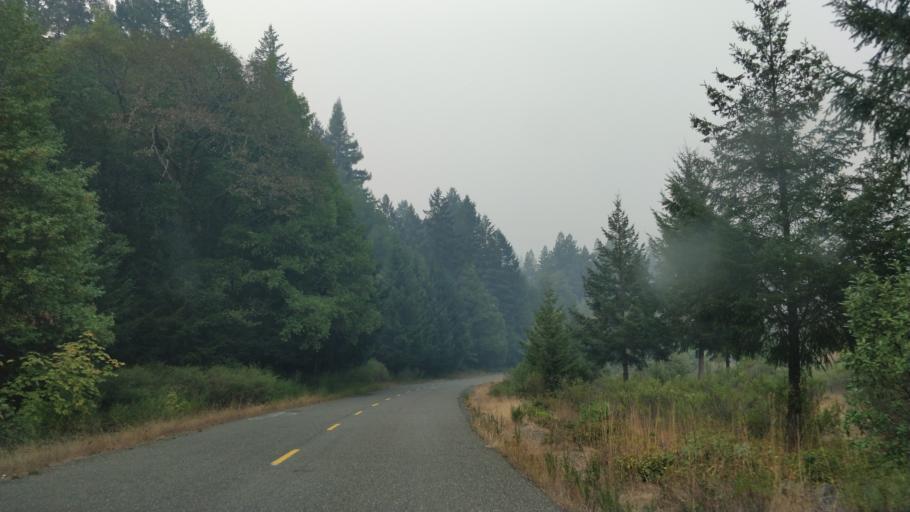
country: US
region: California
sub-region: Humboldt County
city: Rio Dell
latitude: 40.3419
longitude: -124.0267
